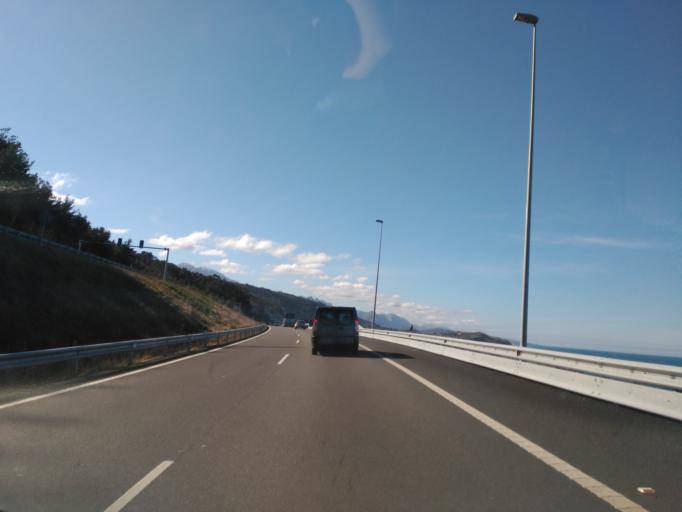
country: ES
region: Cantabria
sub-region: Provincia de Cantabria
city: Tresviso
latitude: 43.3937
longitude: -4.5956
